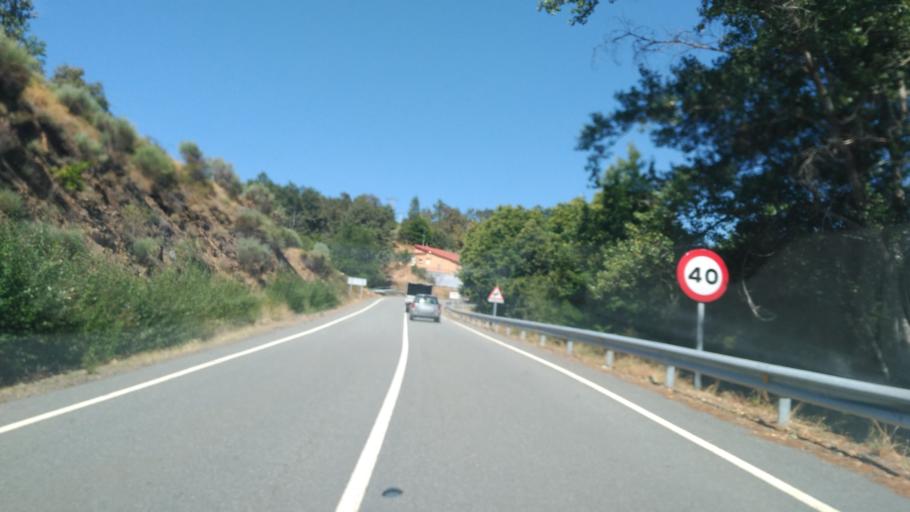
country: ES
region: Castille and Leon
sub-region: Provincia de Salamanca
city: San Martin del Castanar
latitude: 40.5363
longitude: -6.0462
